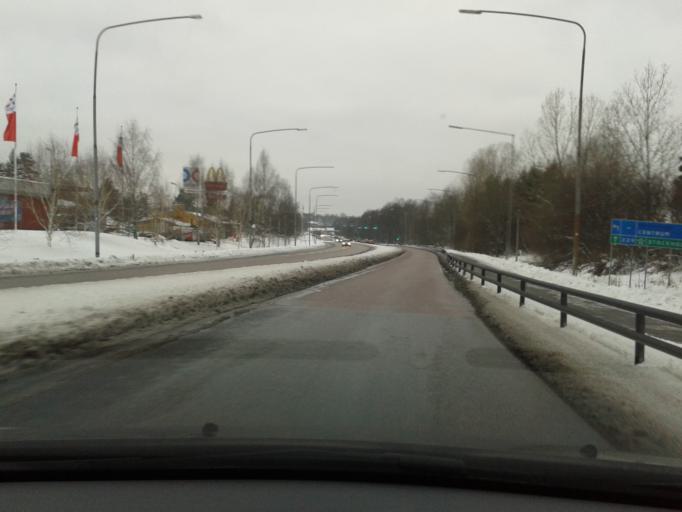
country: SE
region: Stockholm
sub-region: Tyreso Kommun
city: Bollmora
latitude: 59.2498
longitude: 18.2344
